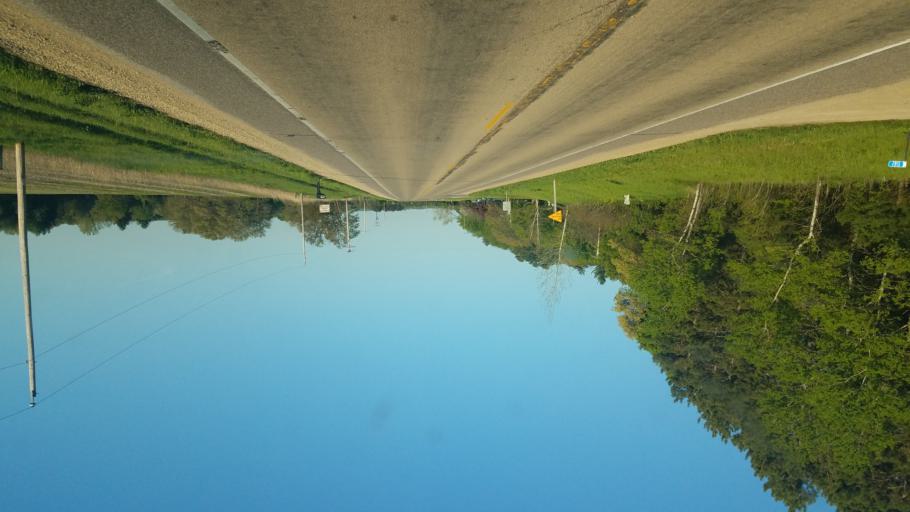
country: US
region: Wisconsin
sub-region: Juneau County
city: Elroy
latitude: 43.6393
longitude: -90.1834
